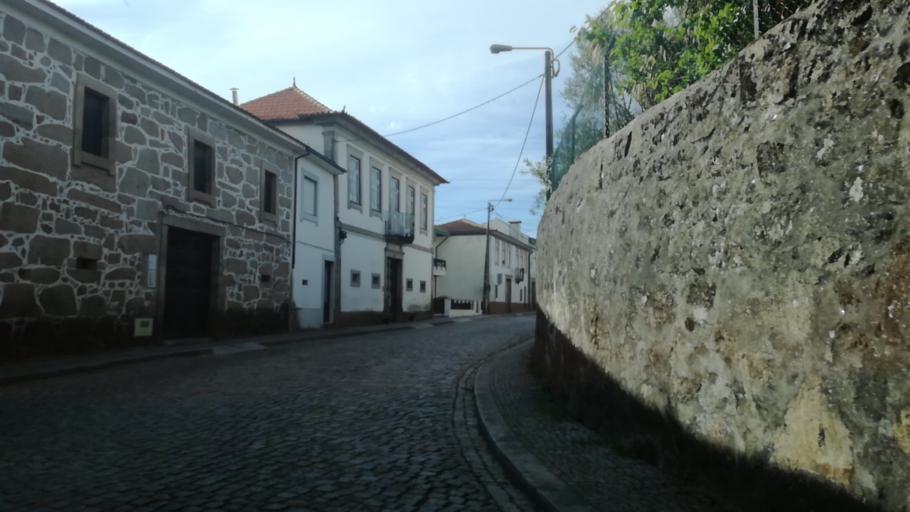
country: PT
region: Porto
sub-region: Maia
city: Nogueira
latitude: 41.2330
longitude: -8.5880
